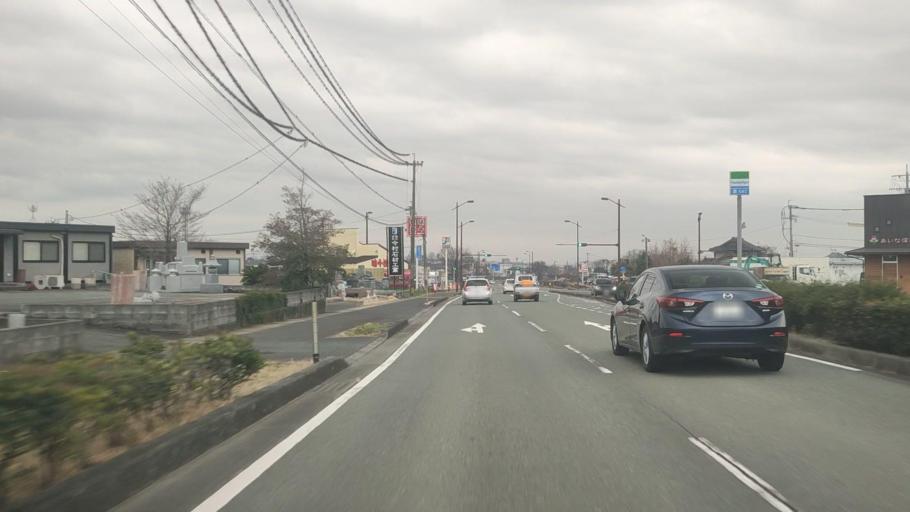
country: JP
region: Kumamoto
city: Ozu
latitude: 32.8316
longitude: 130.7988
